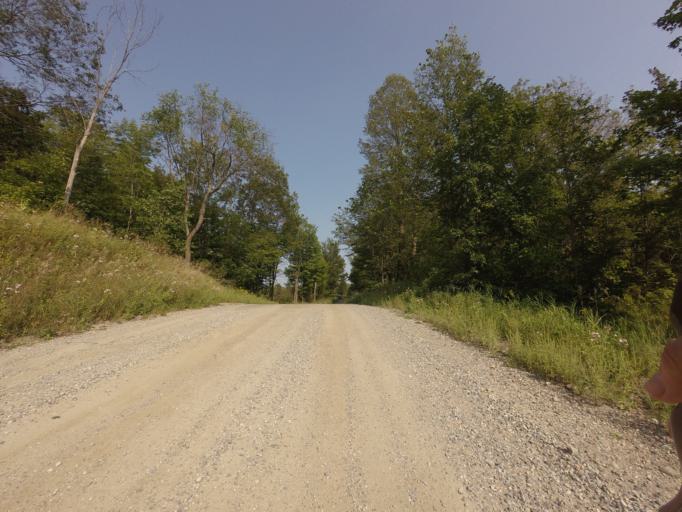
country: CA
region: Ontario
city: Skatepark
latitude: 44.7834
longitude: -76.7912
